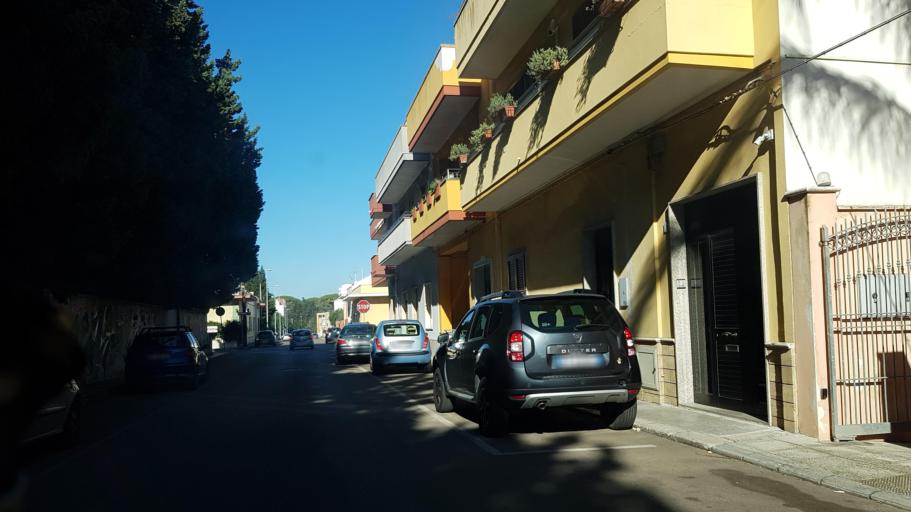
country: IT
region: Apulia
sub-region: Provincia di Lecce
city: Arnesano
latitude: 40.3292
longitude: 18.1016
